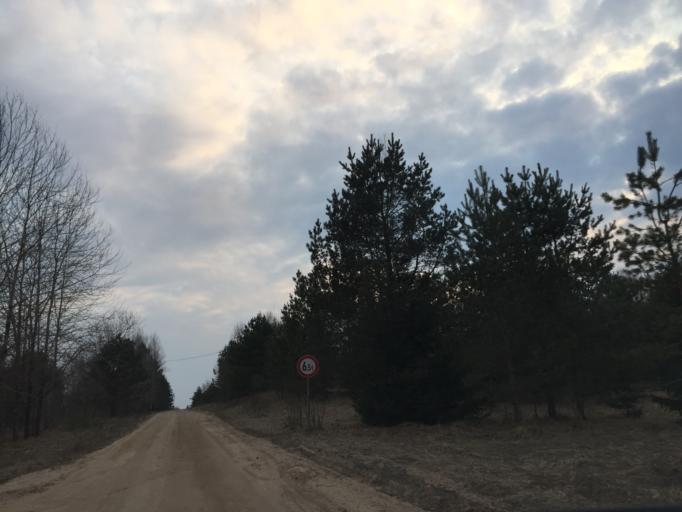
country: LV
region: Raunas
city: Rauna
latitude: 57.1387
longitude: 25.6033
